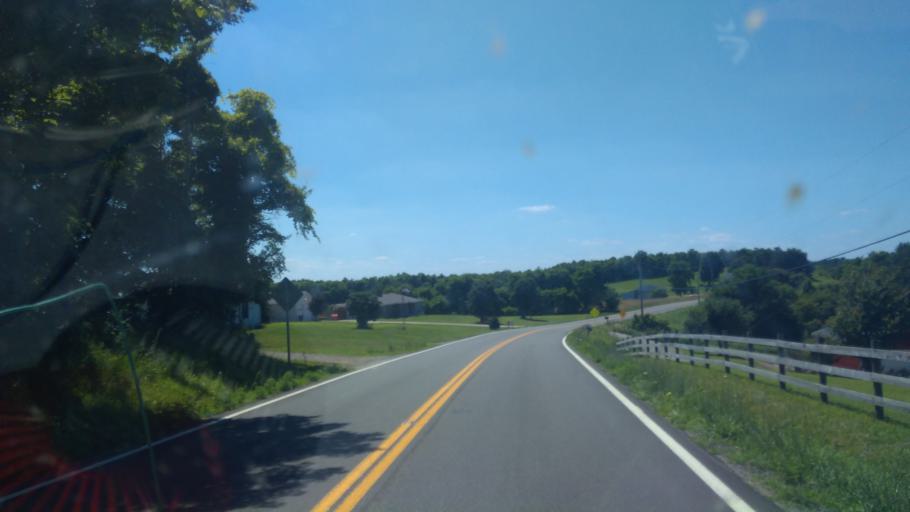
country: US
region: Ohio
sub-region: Carroll County
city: Carrollton
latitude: 40.4934
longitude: -80.9583
